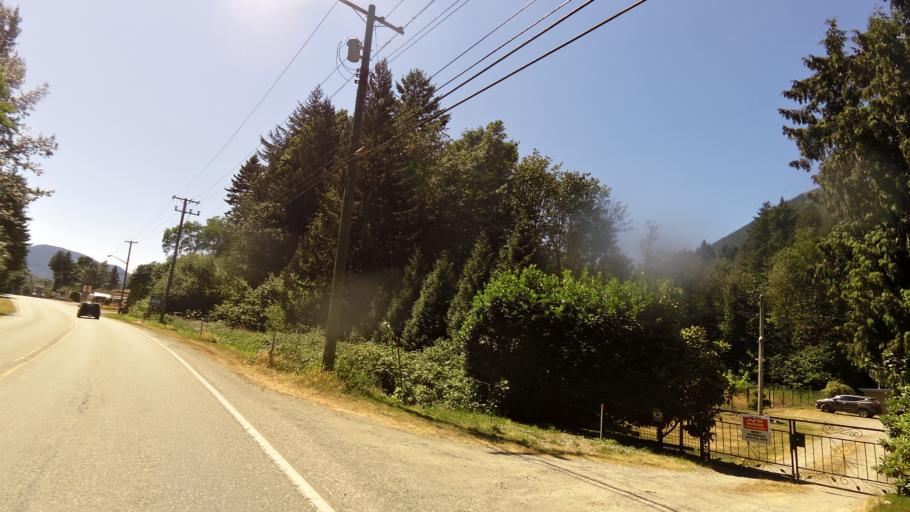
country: CA
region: British Columbia
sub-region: Fraser Valley Regional District
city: Chilliwack
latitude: 49.1919
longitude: -122.0697
